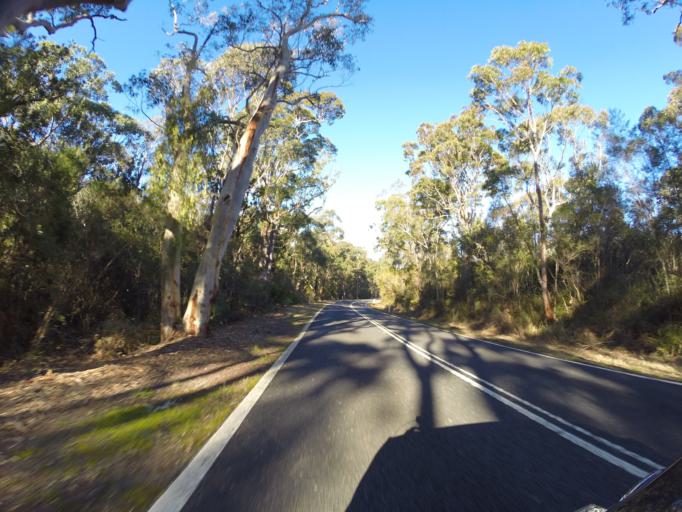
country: AU
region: New South Wales
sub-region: Wollongong
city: Helensburgh
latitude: -34.1470
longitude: 151.0093
